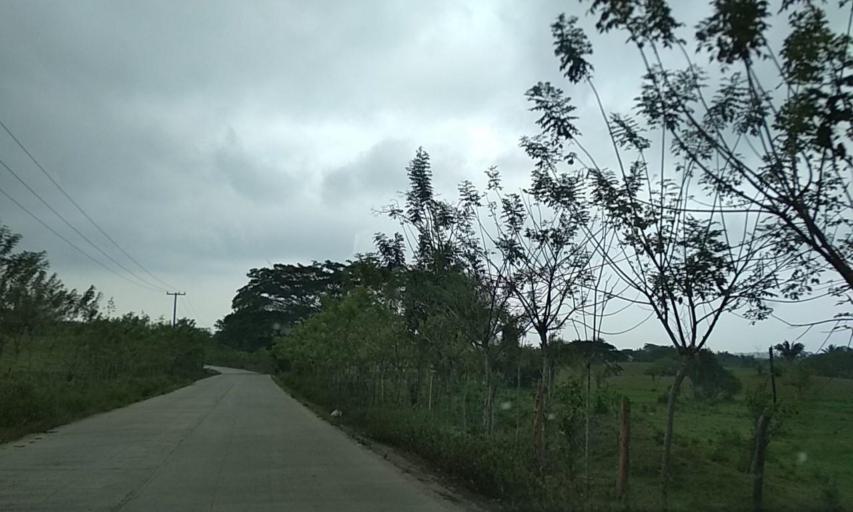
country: MX
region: Tabasco
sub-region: Huimanguillo
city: Francisco Rueda
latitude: 17.6453
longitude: -94.0940
